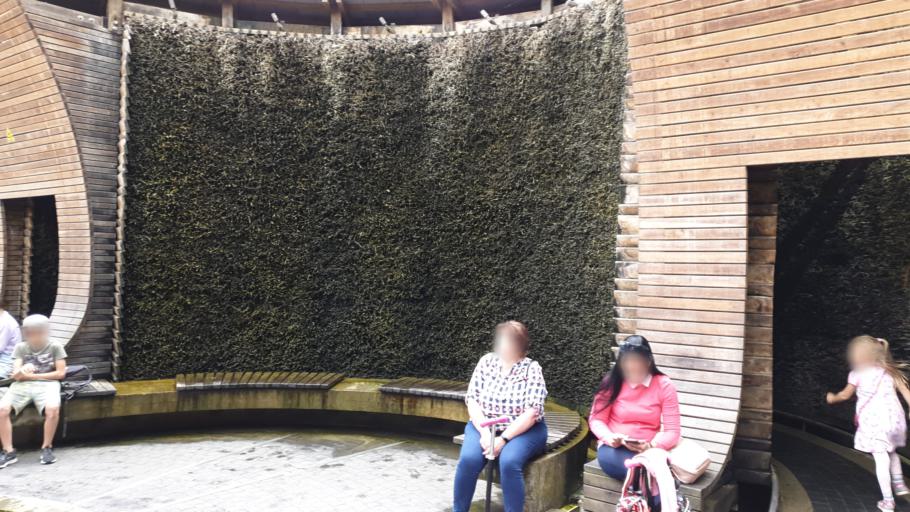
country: LT
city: Birstonas
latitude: 54.6086
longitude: 24.0329
